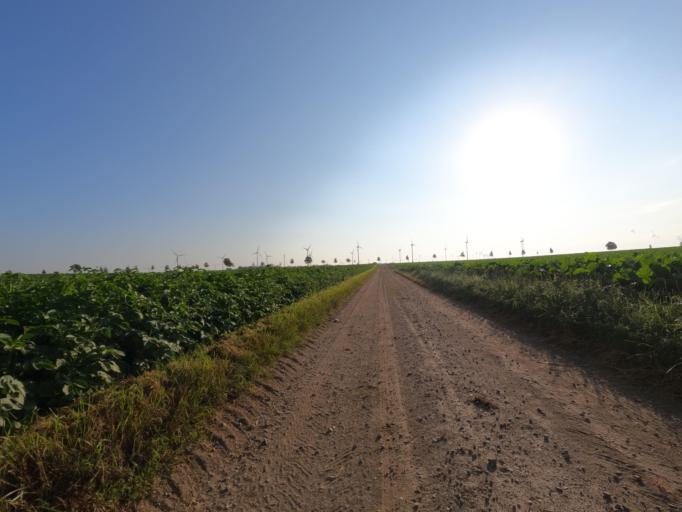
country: DE
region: North Rhine-Westphalia
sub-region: Regierungsbezirk Koln
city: Titz
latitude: 51.0182
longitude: 6.4708
